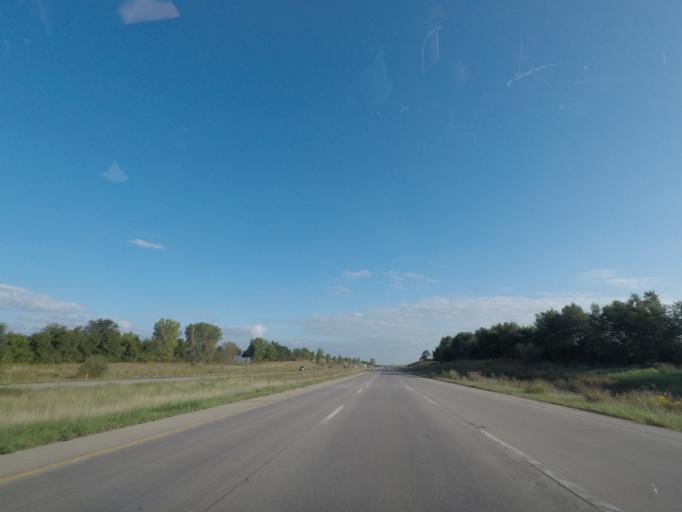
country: US
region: Iowa
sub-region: Warren County
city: Carlisle
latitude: 41.5293
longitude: -93.5191
